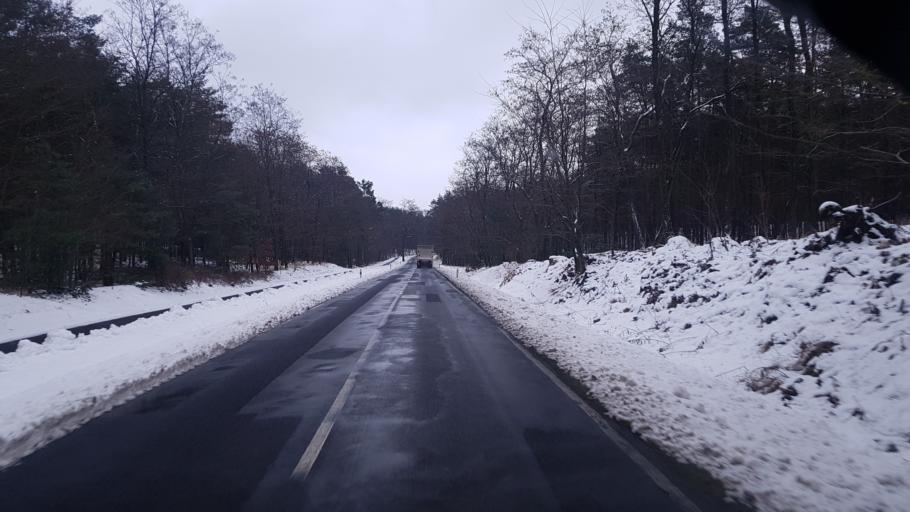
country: DE
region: Brandenburg
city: Lawitz
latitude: 52.0828
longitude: 14.5103
